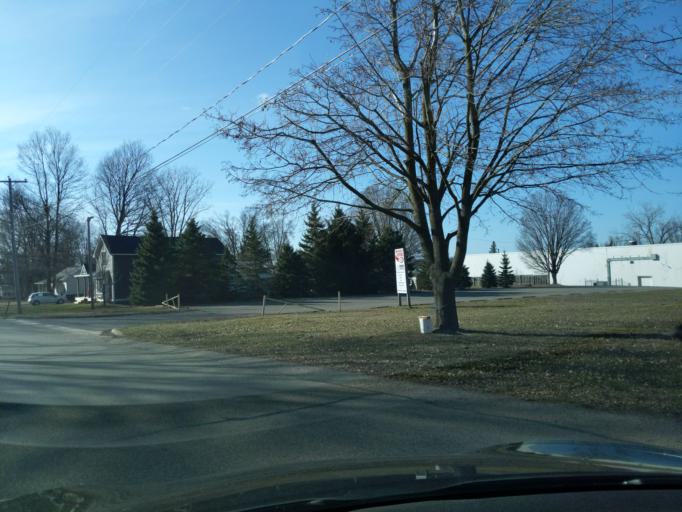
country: US
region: Michigan
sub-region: Ionia County
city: Saranac
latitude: 42.9298
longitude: -85.2003
